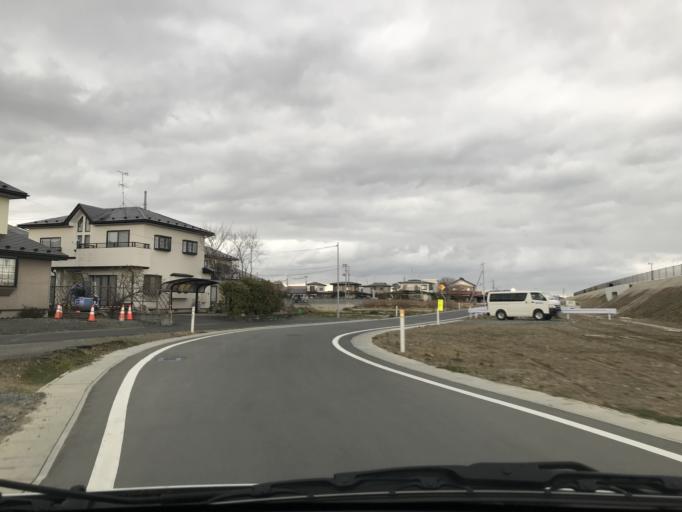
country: JP
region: Iwate
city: Mizusawa
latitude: 39.1276
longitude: 141.1624
